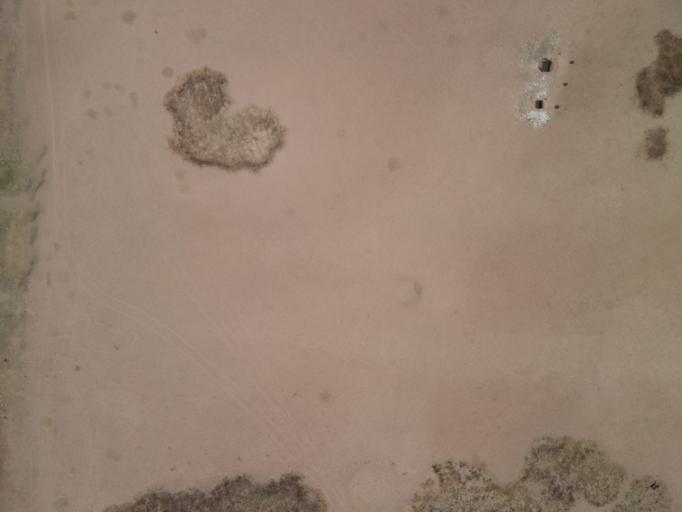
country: BO
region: La Paz
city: Batallas
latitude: -16.3556
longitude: -68.6310
